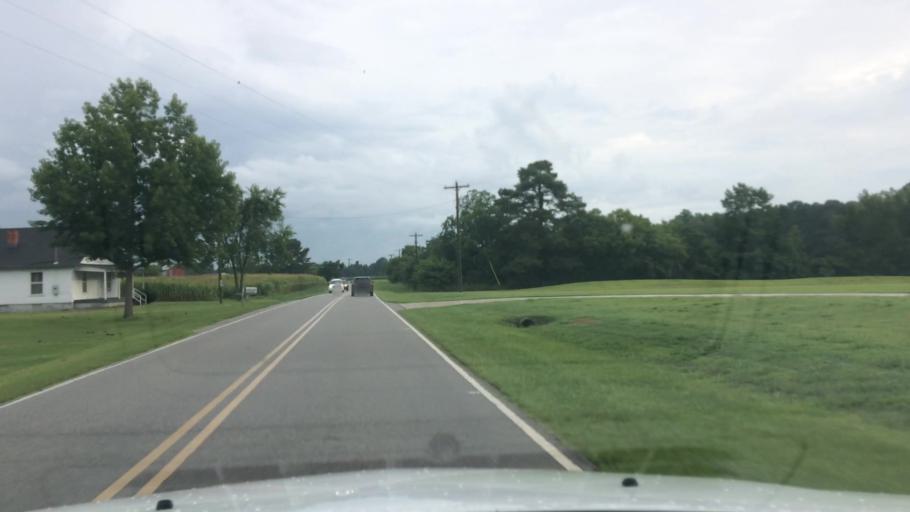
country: US
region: North Carolina
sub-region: Pitt County
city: Farmville
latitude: 35.5736
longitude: -77.5498
